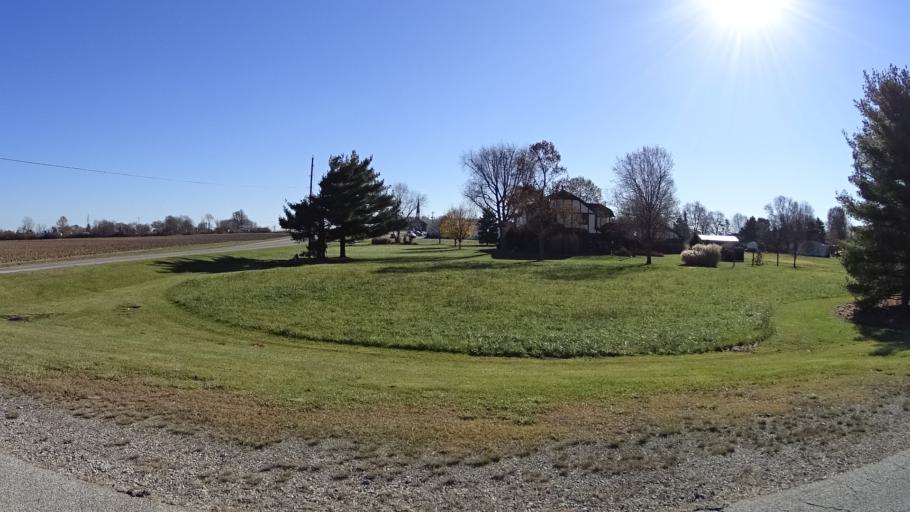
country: US
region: Ohio
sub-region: Lorain County
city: Elyria
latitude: 41.3773
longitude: -82.1649
